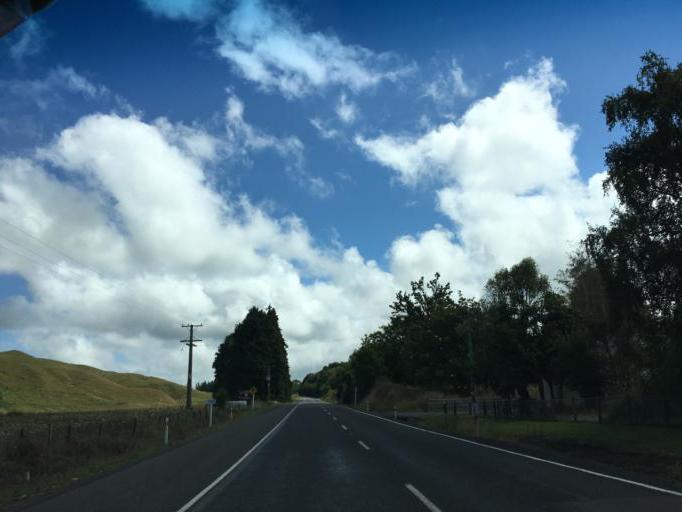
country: NZ
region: Hawke's Bay
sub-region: Wairoa District
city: Wairoa
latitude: -39.0627
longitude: 177.0360
